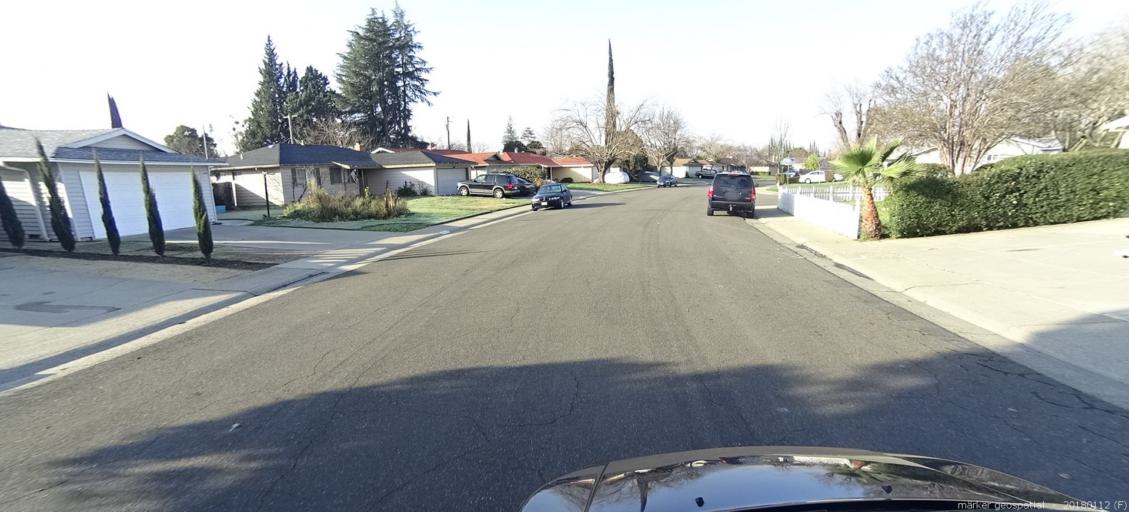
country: US
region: California
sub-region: Sacramento County
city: Rancho Cordova
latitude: 38.6108
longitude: -121.2868
